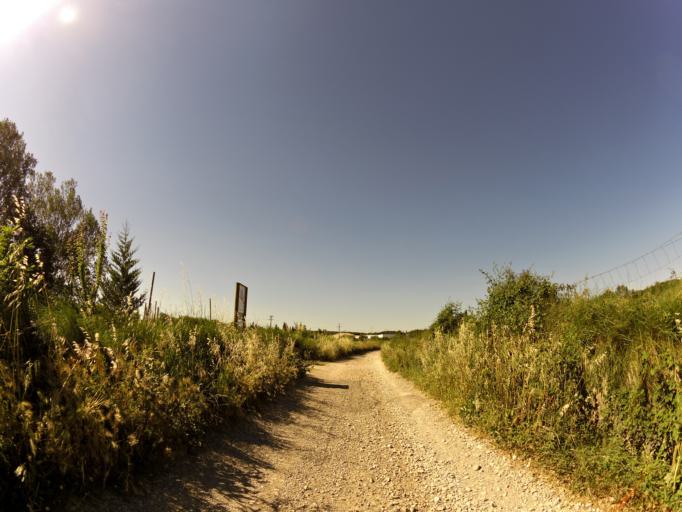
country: FR
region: Languedoc-Roussillon
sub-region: Departement de l'Herault
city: Villetelle
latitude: 43.7390
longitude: 4.1422
